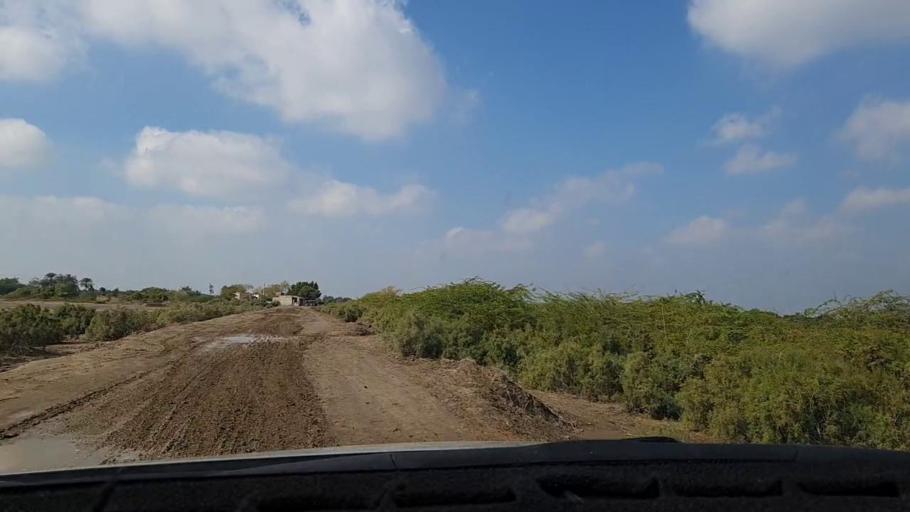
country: PK
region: Sindh
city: Tando Mittha Khan
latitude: 25.7730
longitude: 69.2597
